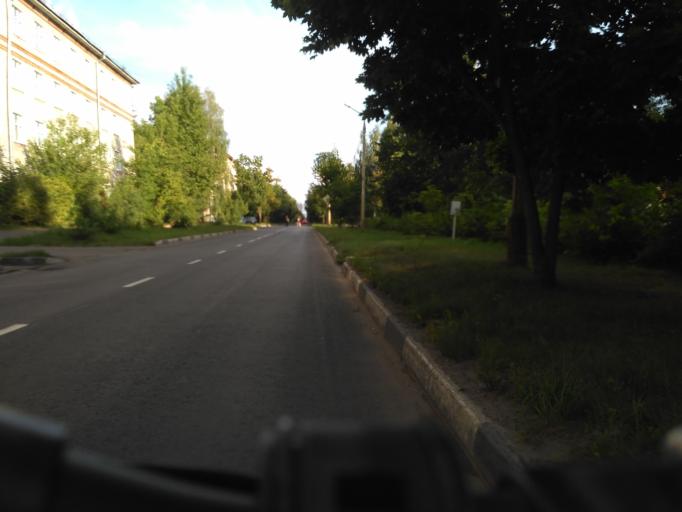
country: RU
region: Moskovskaya
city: Dubna
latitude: 56.7519
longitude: 37.1982
